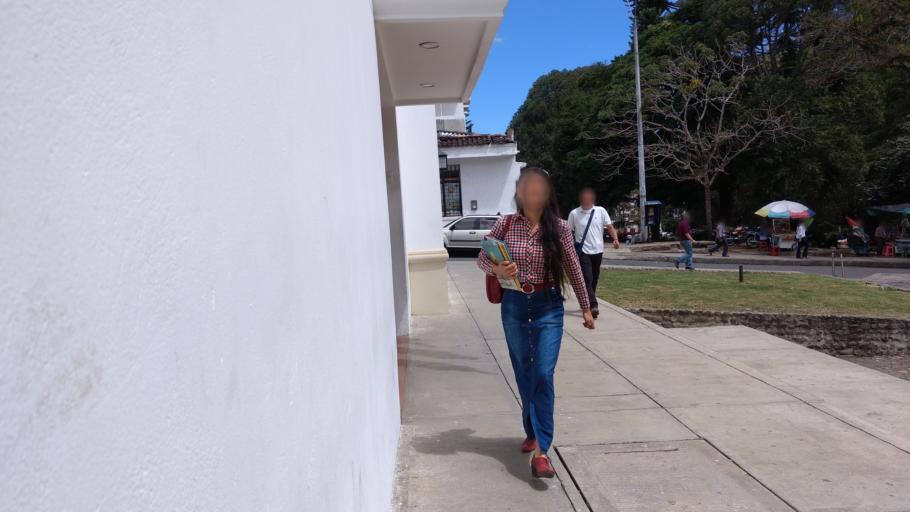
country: CO
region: Cauca
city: Popayan
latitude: 2.4440
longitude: -76.6058
